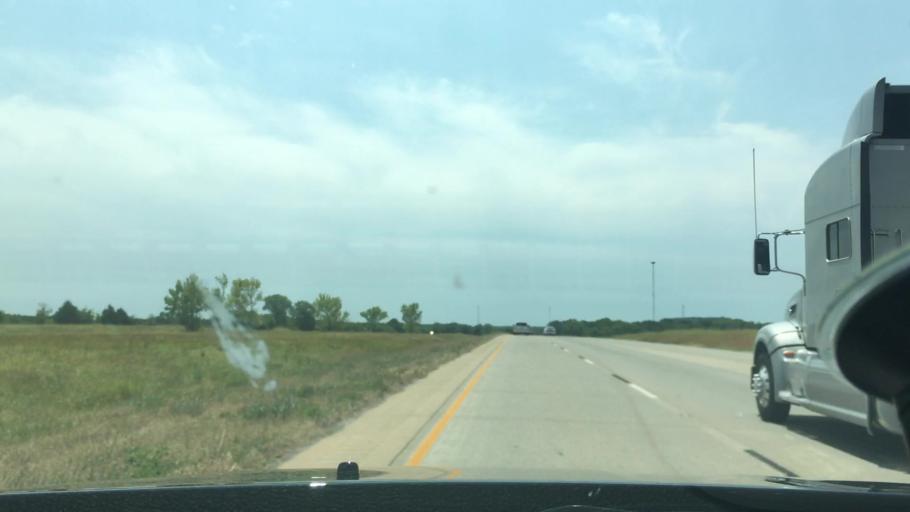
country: US
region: Oklahoma
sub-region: Love County
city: Marietta
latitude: 34.0244
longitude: -97.1476
